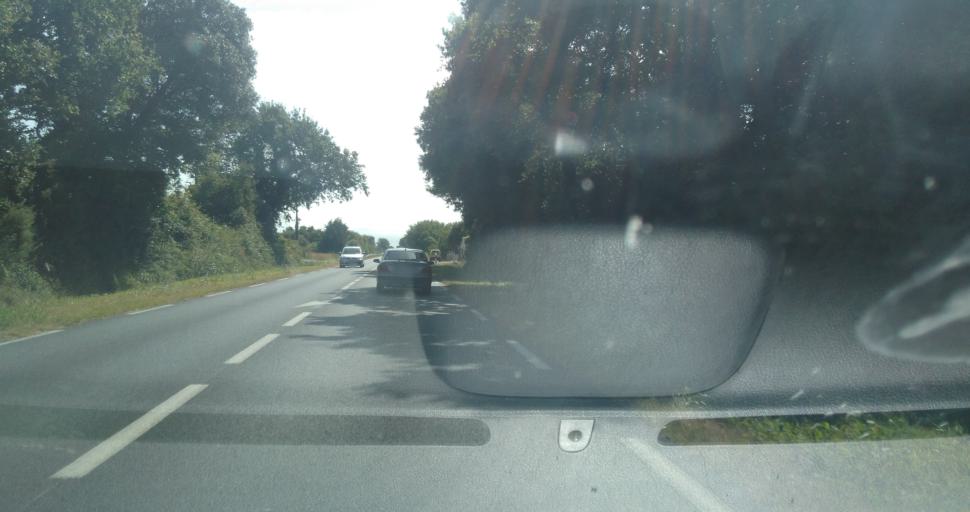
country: FR
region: Pays de la Loire
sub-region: Departement de la Vendee
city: Sainte-Foy
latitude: 46.4777
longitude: -1.6759
